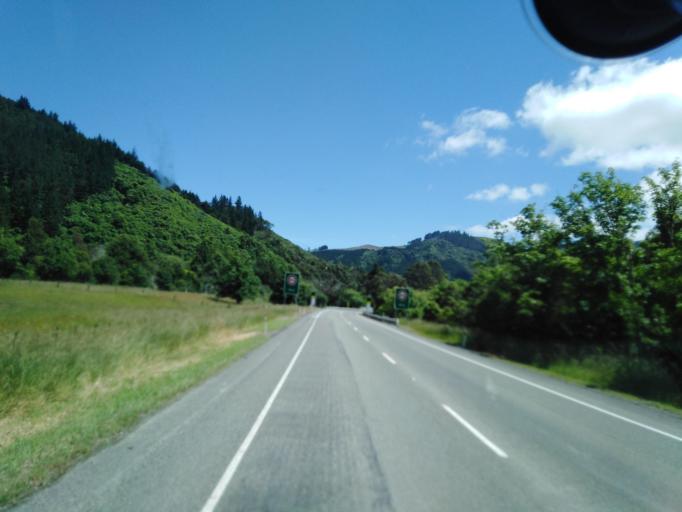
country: NZ
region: Nelson
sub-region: Nelson City
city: Nelson
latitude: -41.2188
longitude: 173.3971
